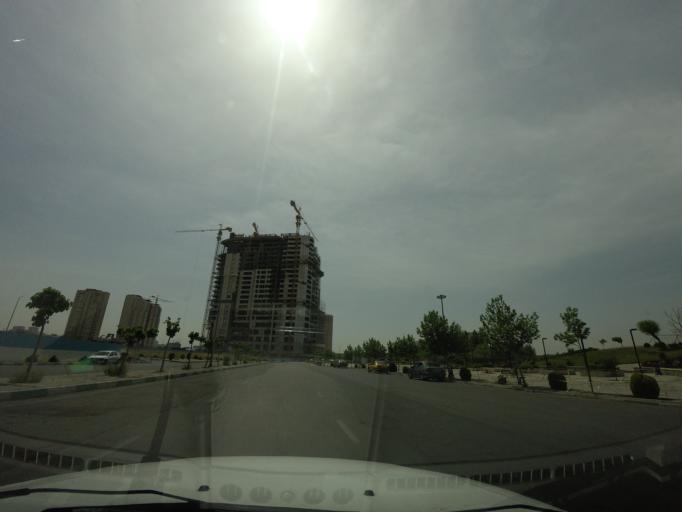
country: IR
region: Tehran
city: Shahr-e Qods
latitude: 35.7483
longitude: 51.2217
